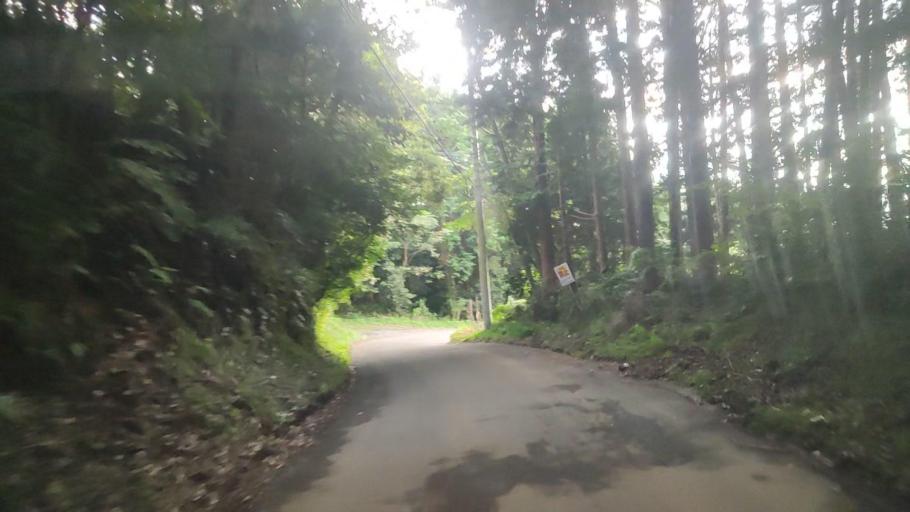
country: JP
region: Shizuoka
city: Mishima
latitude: 35.1219
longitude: 138.9814
